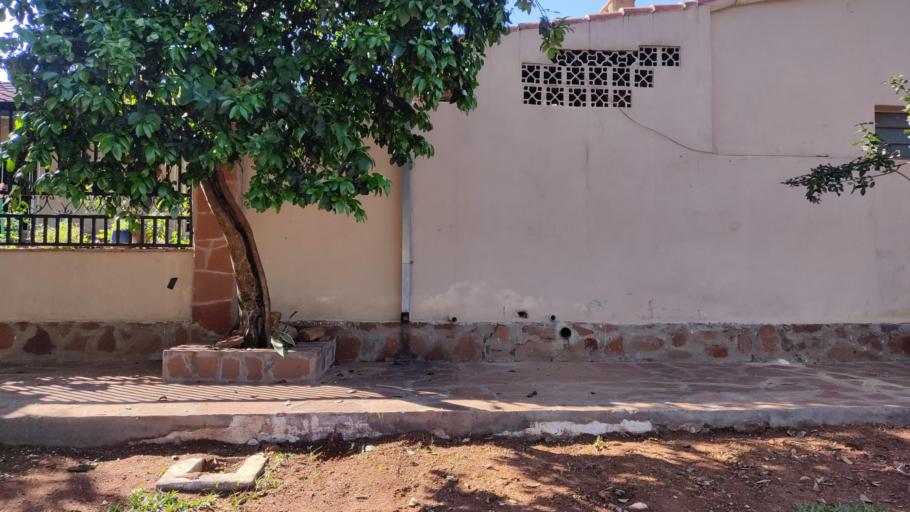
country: PY
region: Misiones
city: San Juan Bautista
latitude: -26.6665
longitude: -57.1377
